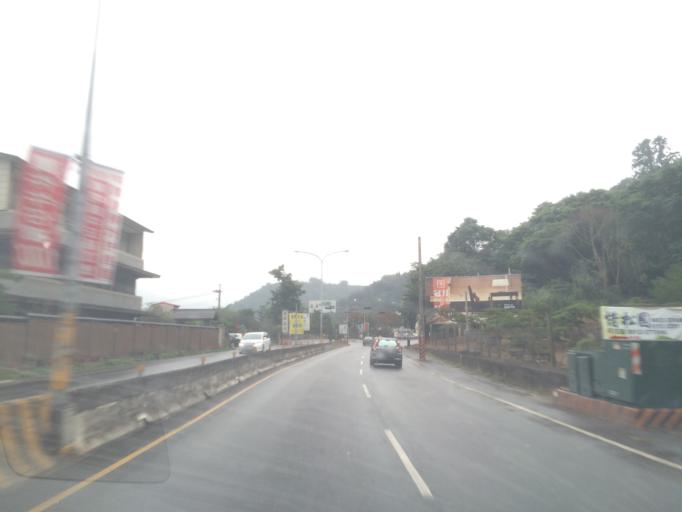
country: TW
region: Taiwan
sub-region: Nantou
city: Puli
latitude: 23.9691
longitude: 120.9309
